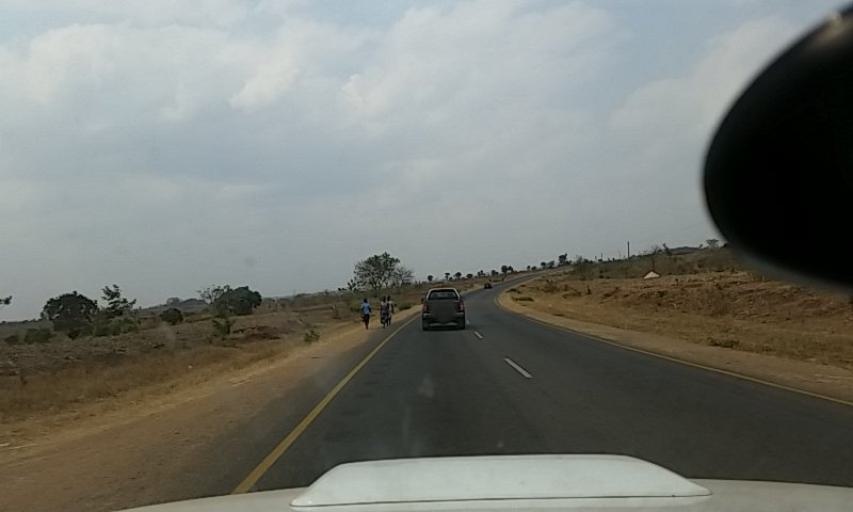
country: MW
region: Central Region
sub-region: Lilongwe District
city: Lilongwe
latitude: -13.8458
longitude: 33.8401
